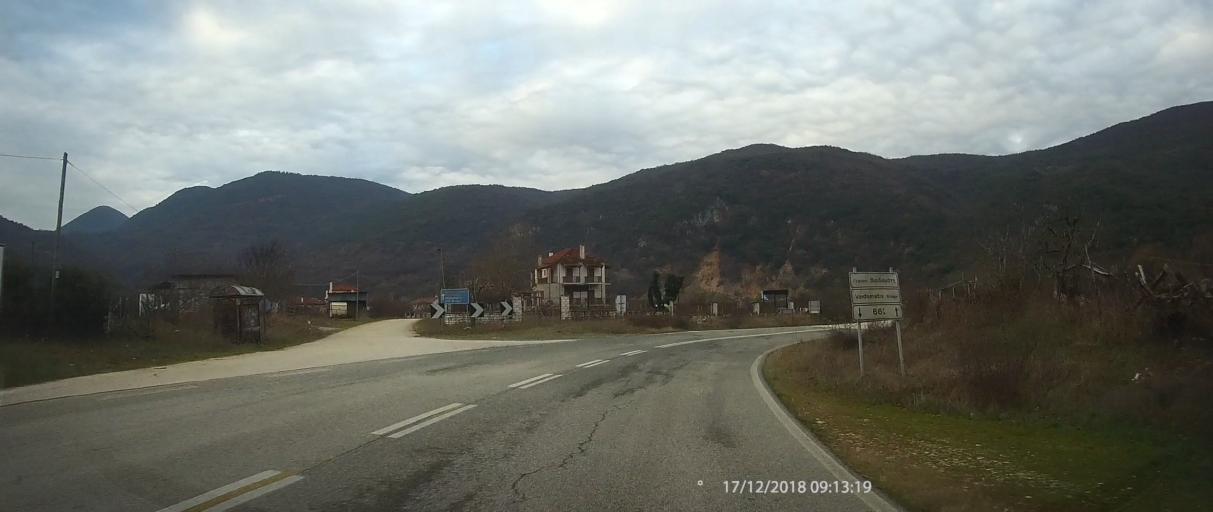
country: GR
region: Epirus
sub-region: Nomos Ioanninon
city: Kalpaki
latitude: 39.9735
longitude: 20.6602
